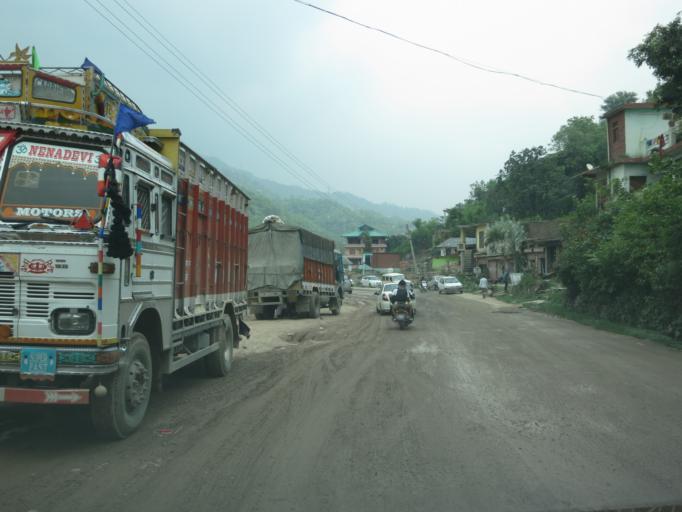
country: IN
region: Himachal Pradesh
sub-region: Mandi
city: Sundarnagar
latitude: 31.4569
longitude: 76.8610
